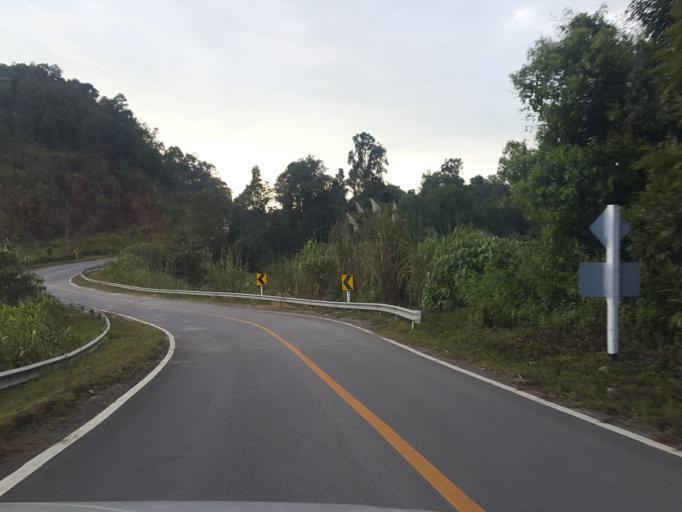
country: TH
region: Mae Hong Son
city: Khun Yuam
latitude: 18.7991
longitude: 98.0694
